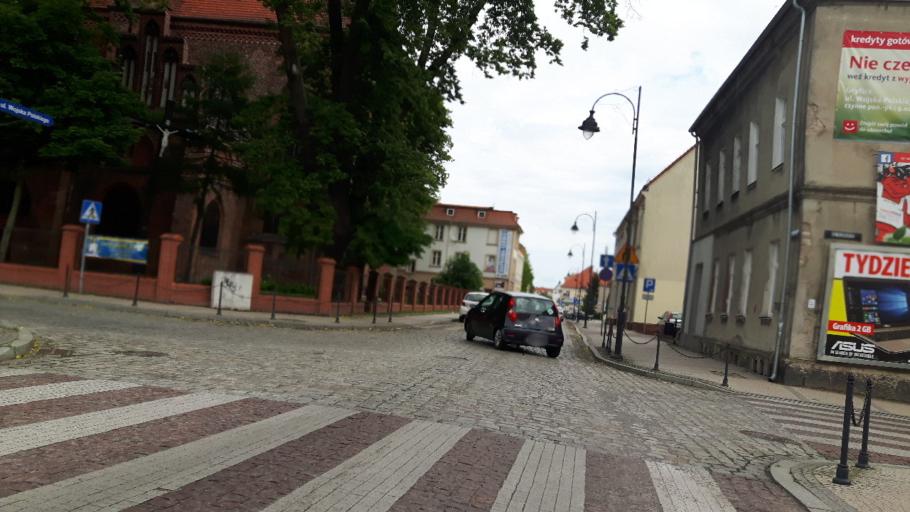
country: PL
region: West Pomeranian Voivodeship
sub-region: Powiat gryficki
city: Gryfice
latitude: 53.9131
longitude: 15.1990
